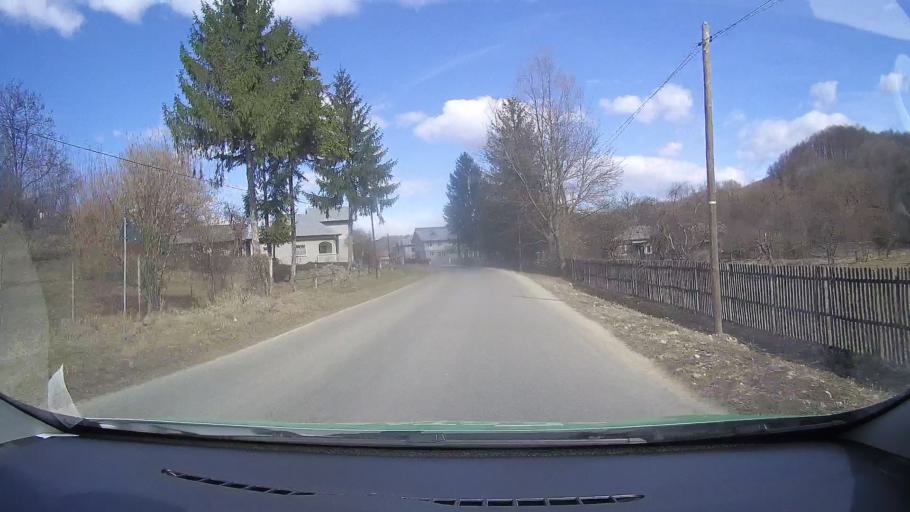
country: RO
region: Dambovita
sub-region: Comuna Vulcana Bai
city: Vulcana Bai
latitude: 45.0634
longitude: 25.3778
